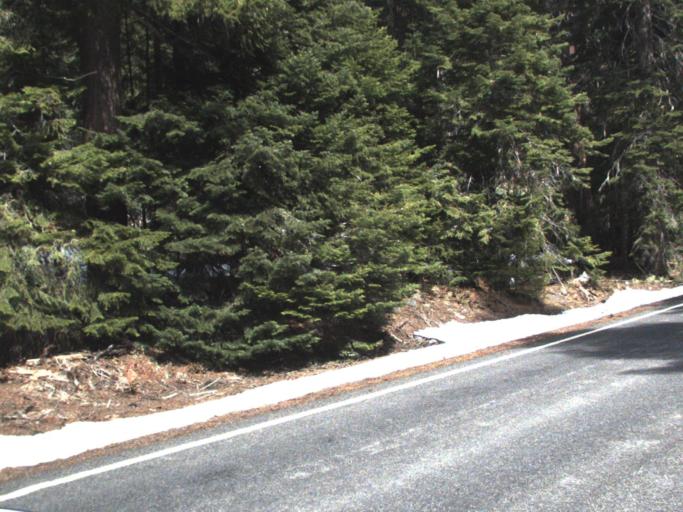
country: US
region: Washington
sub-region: Kittitas County
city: Cle Elum
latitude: 46.9755
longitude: -121.1853
